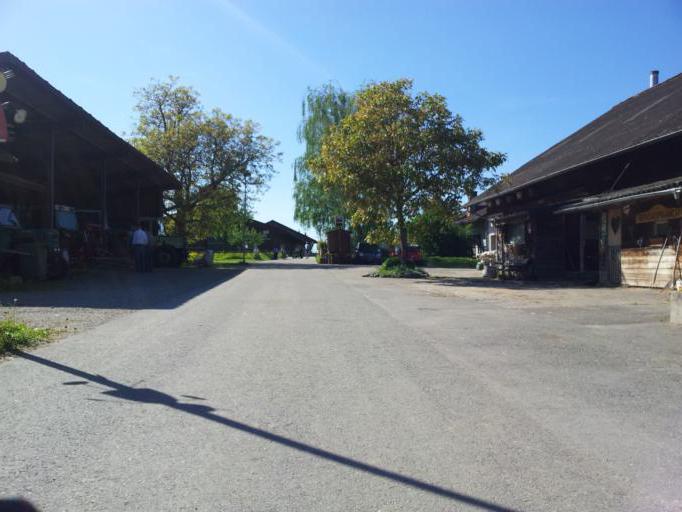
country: CH
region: Zurich
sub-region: Bezirk Dietikon
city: Schlieren / Boden
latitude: 47.3921
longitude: 8.4606
